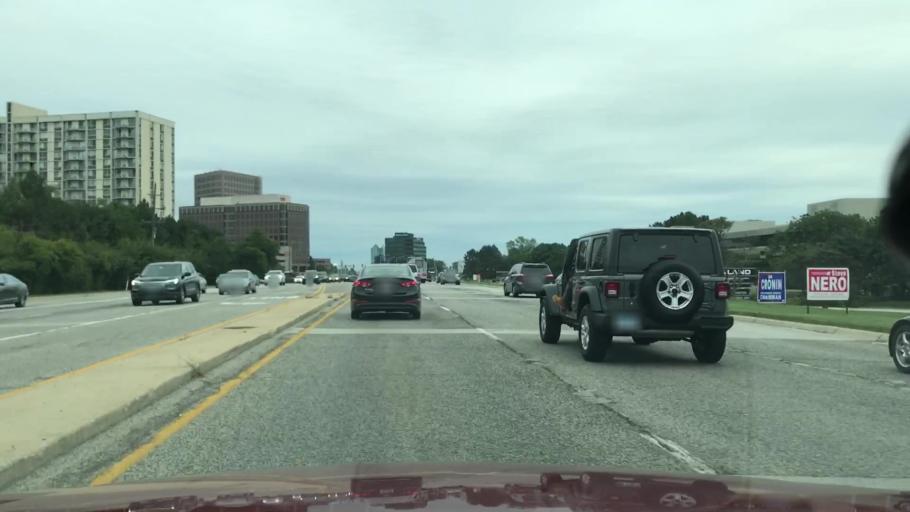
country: US
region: Illinois
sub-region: DuPage County
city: Oakbrook Terrace
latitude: 41.8434
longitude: -87.9898
